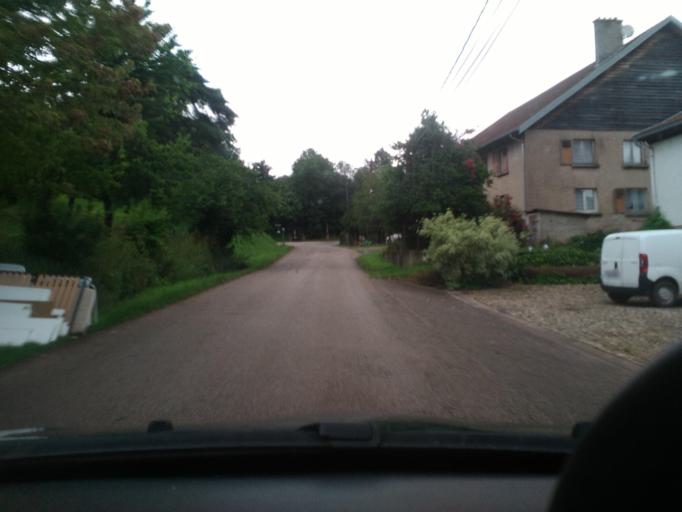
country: FR
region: Lorraine
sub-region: Departement des Vosges
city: Saint-Michel-sur-Meurthe
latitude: 48.3243
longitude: 6.9187
